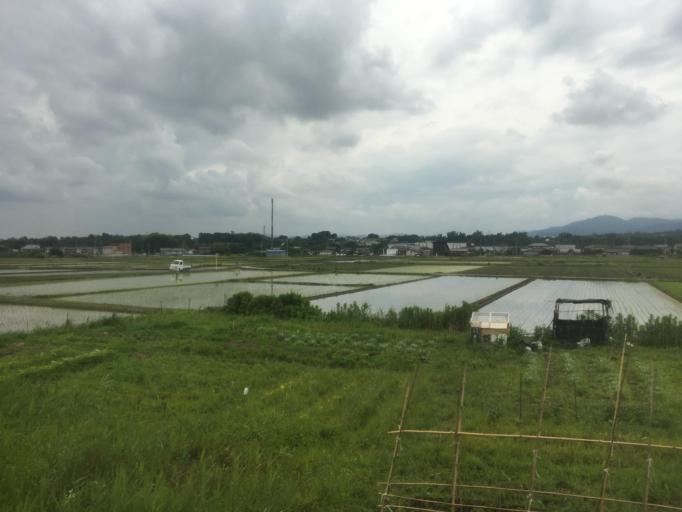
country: JP
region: Gunma
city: Yoshii
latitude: 36.2690
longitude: 139.0284
